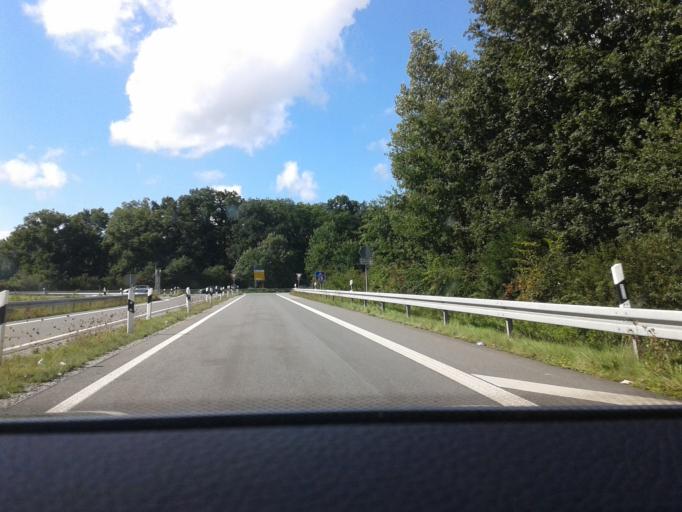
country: DE
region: North Rhine-Westphalia
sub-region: Regierungsbezirk Dusseldorf
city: Uedem
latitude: 51.6371
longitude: 6.2926
